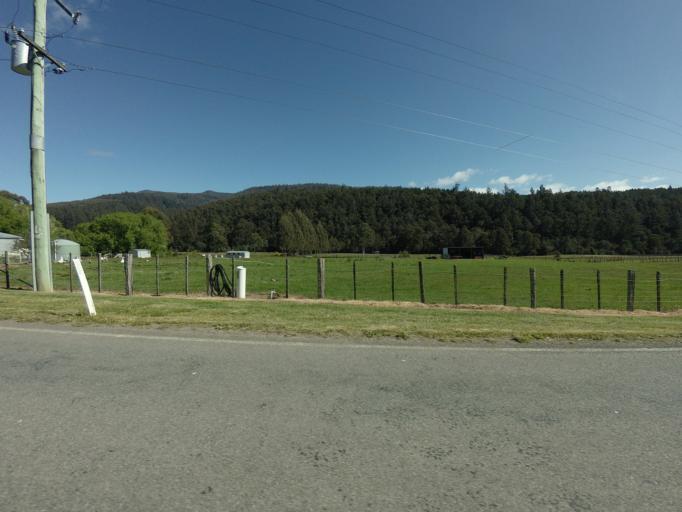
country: AU
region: Tasmania
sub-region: Derwent Valley
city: New Norfolk
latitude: -42.7236
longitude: 146.6775
